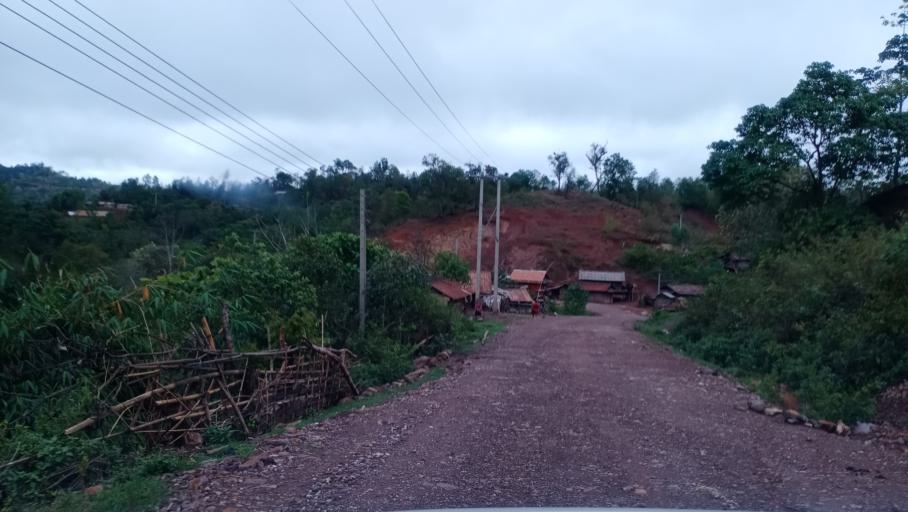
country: LA
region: Phongsali
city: Phongsali
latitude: 21.3390
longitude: 102.0785
